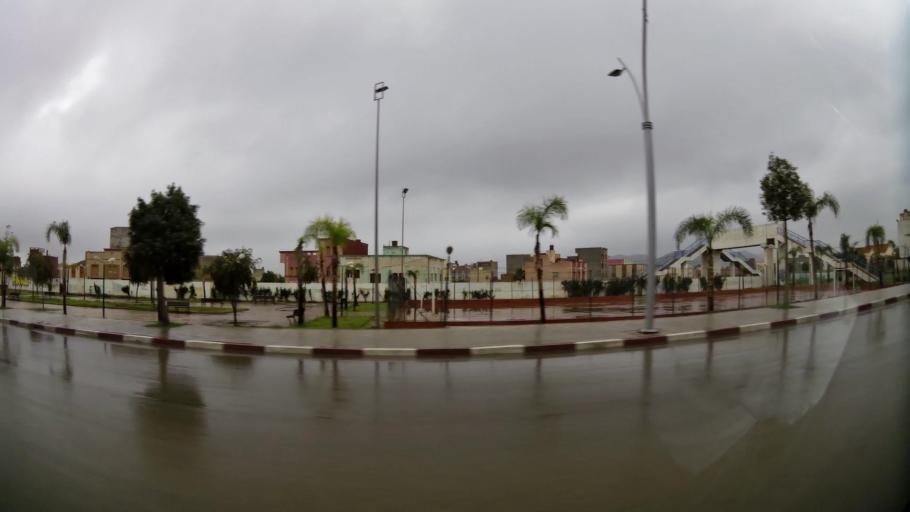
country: MA
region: Oriental
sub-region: Nador
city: Nador
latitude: 35.1573
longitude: -2.9735
